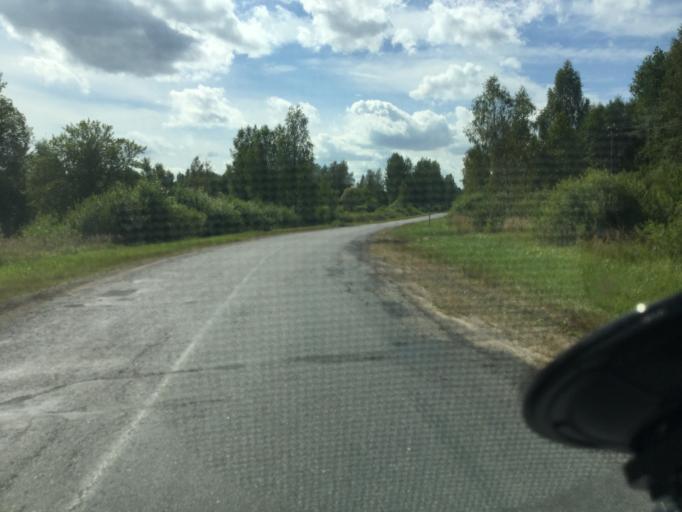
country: BY
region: Vitebsk
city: Chashniki
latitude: 55.2872
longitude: 29.3612
